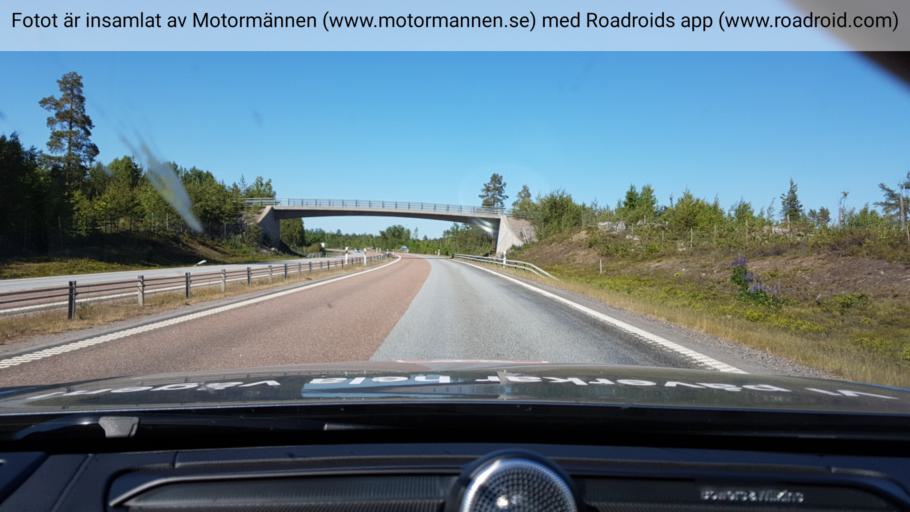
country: SE
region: Gaevleborg
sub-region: Soderhamns Kommun
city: Soderhamn
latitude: 61.3116
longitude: 17.0351
